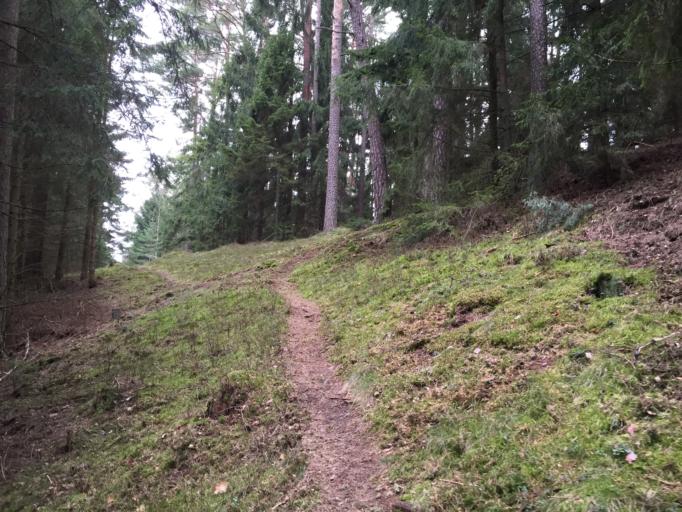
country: LT
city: Neringa
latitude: 55.5382
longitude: 21.1137
